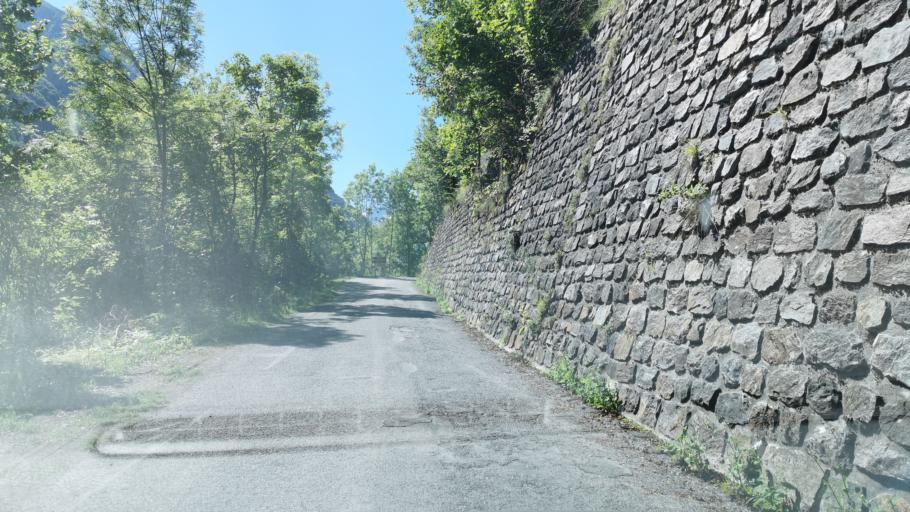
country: IT
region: Piedmont
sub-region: Provincia di Cuneo
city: Entracque
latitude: 44.2087
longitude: 7.3779
